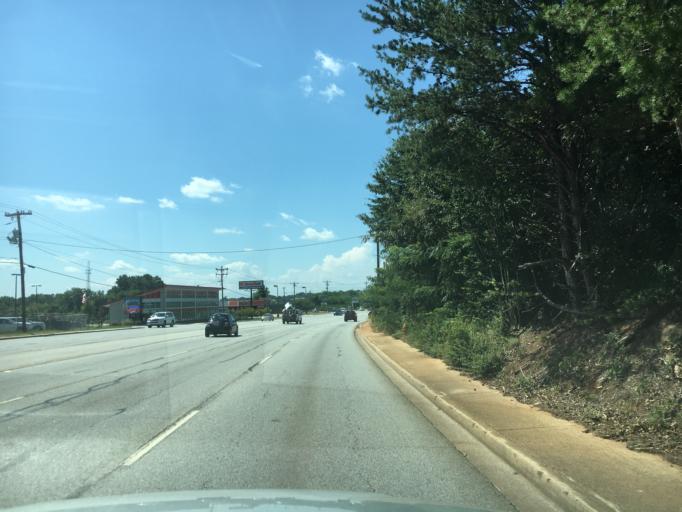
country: US
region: South Carolina
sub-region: Greenville County
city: Sans Souci
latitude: 34.8870
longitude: -82.3942
